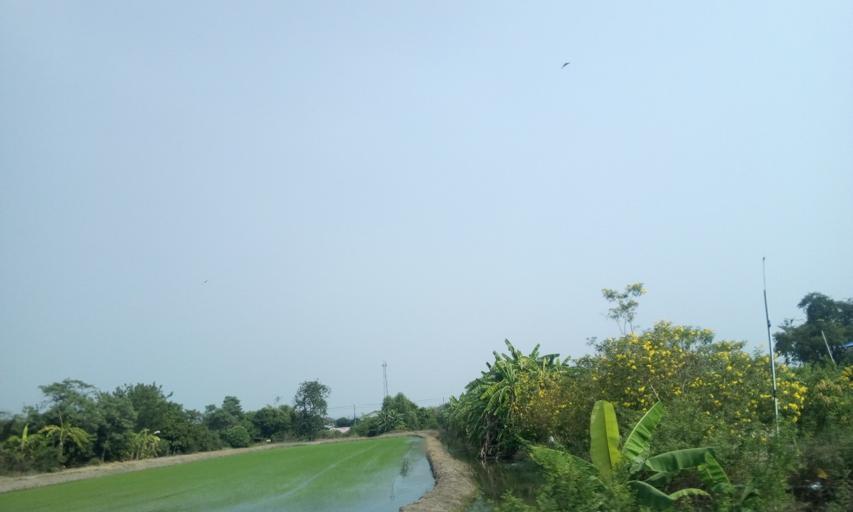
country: TH
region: Pathum Thani
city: Lam Luk Ka
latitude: 13.9589
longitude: 100.7253
